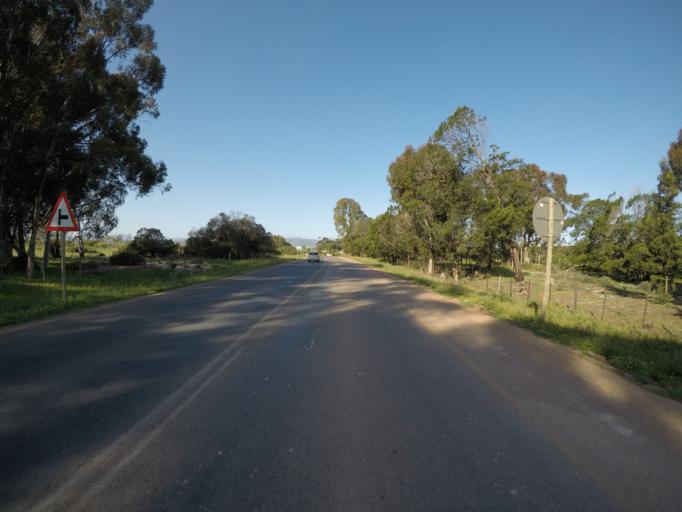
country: ZA
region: Western Cape
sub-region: City of Cape Town
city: Kraaifontein
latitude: -33.7667
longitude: 18.7860
